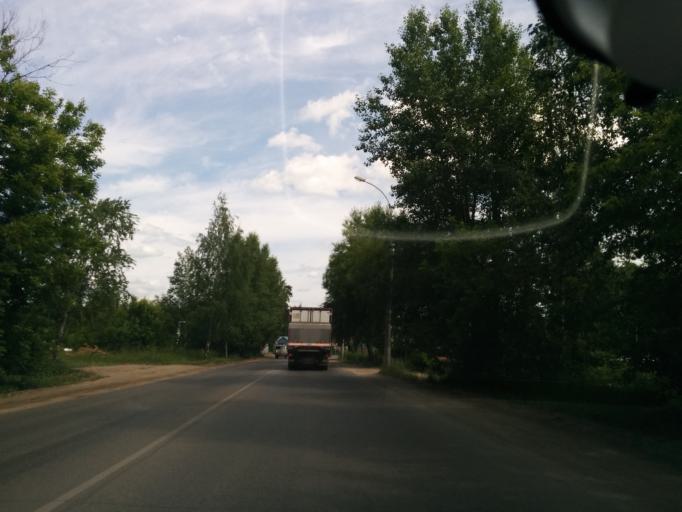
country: RU
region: Perm
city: Overyata
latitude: 58.0193
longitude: 55.9730
